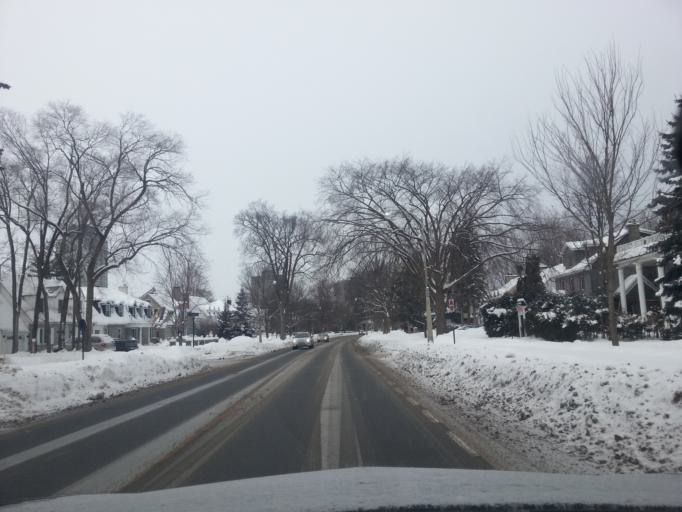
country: CA
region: Ontario
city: Ottawa
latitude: 45.3976
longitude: -75.7430
